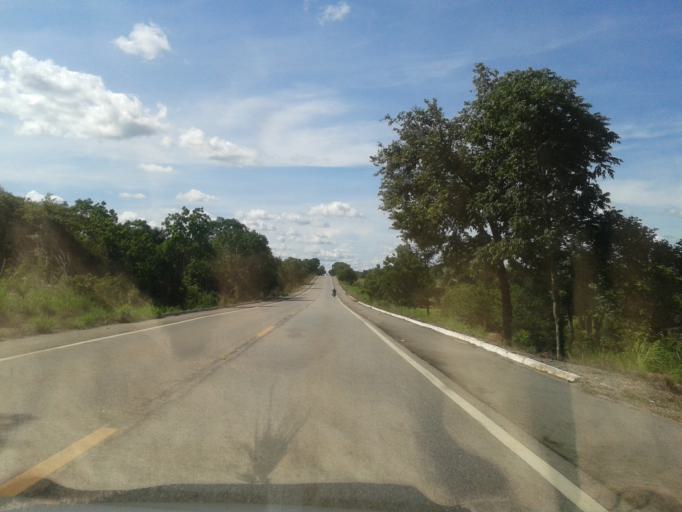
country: BR
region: Goias
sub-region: Mozarlandia
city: Mozarlandia
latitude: -15.2745
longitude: -50.4808
